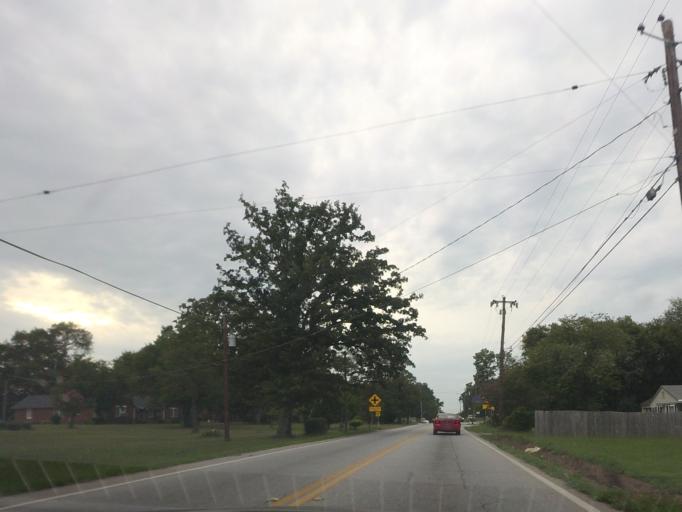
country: US
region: Georgia
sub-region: Bibb County
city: Macon
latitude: 32.8131
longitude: -83.5174
